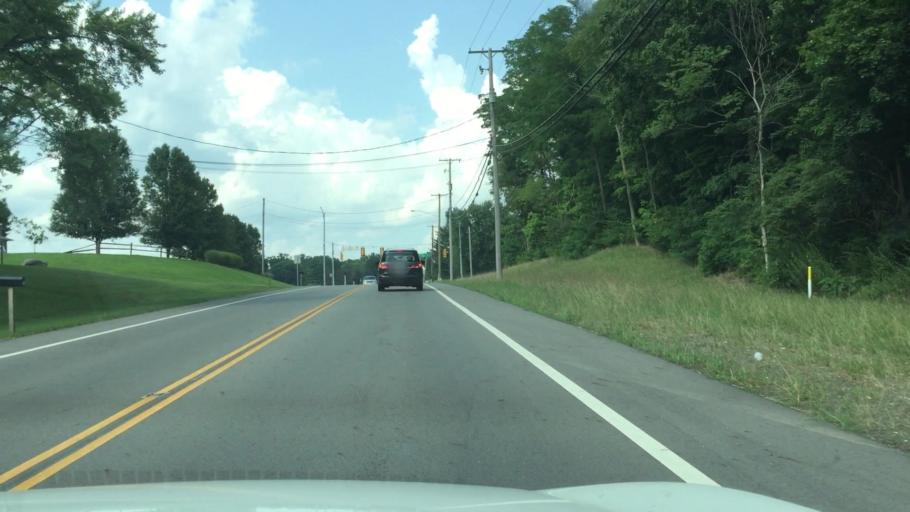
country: US
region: Ohio
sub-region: Clark County
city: Northridge
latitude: 39.9833
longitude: -83.7833
